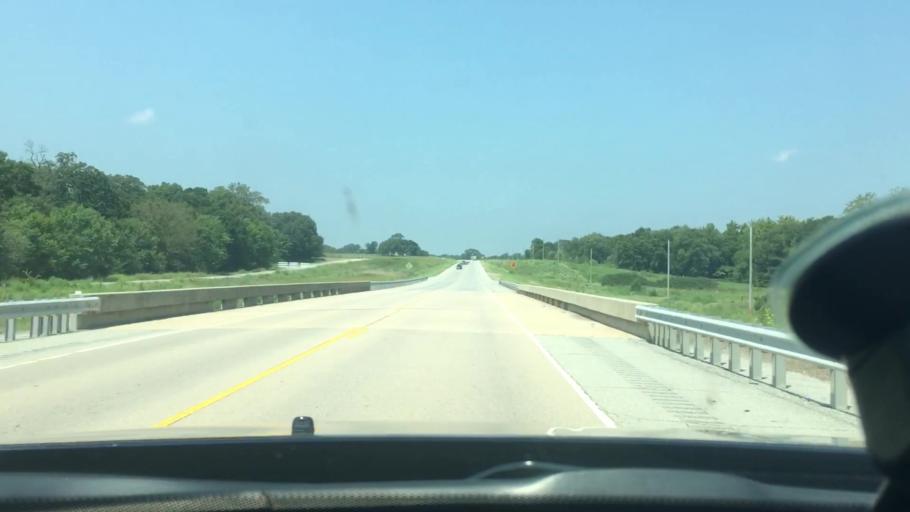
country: US
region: Oklahoma
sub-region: Atoka County
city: Atoka
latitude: 34.2909
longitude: -95.9718
